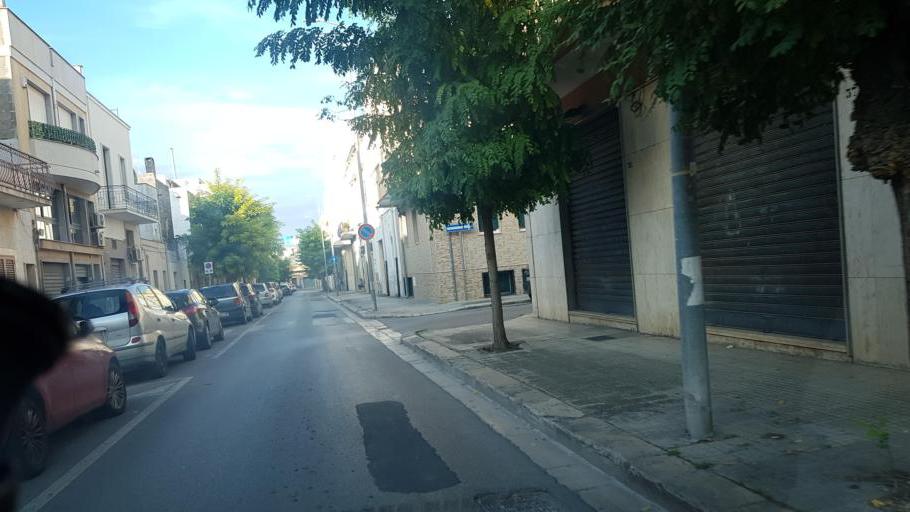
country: IT
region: Apulia
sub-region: Provincia di Brindisi
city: Francavilla Fontana
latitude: 40.5307
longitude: 17.5865
